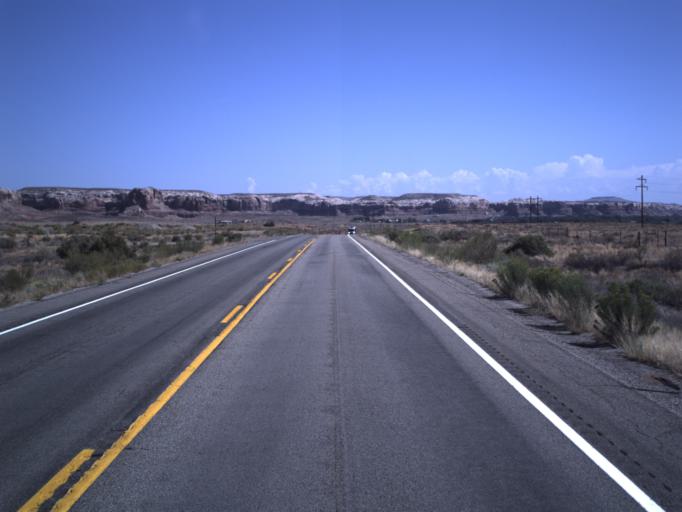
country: US
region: Utah
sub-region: San Juan County
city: Blanding
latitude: 37.2727
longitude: -109.5936
